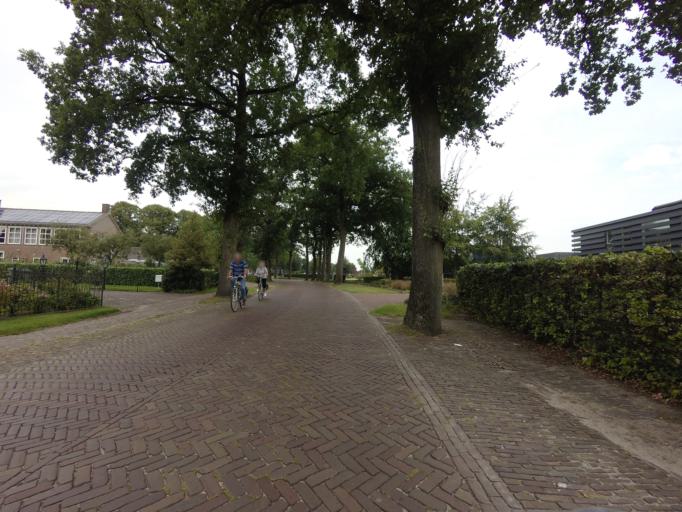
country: NL
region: Drenthe
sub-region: Gemeente Westerveld
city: Dwingeloo
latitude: 52.8371
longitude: 6.3651
